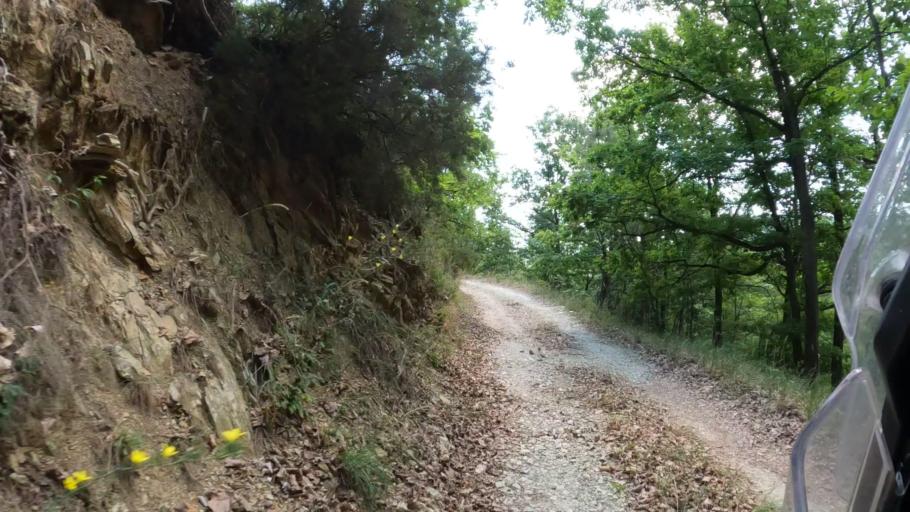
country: IT
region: Piedmont
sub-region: Provincia di Alessandria
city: Cassinelle-Concentrico
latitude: 44.5673
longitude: 8.5685
